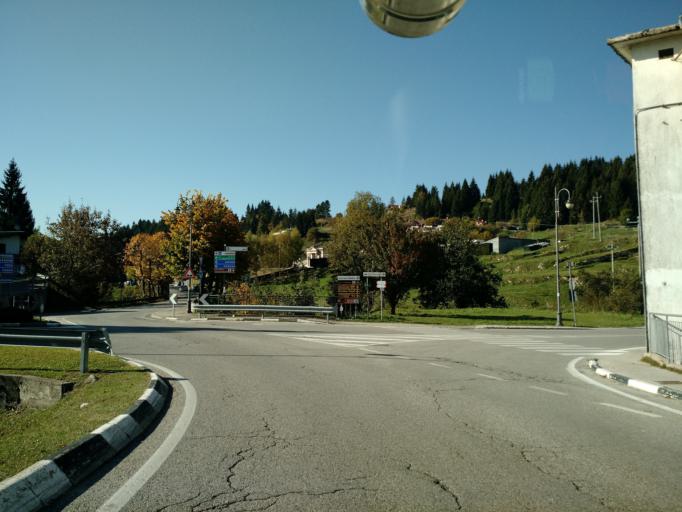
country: IT
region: Veneto
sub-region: Provincia di Vicenza
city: Gallio
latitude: 45.8928
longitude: 11.5444
